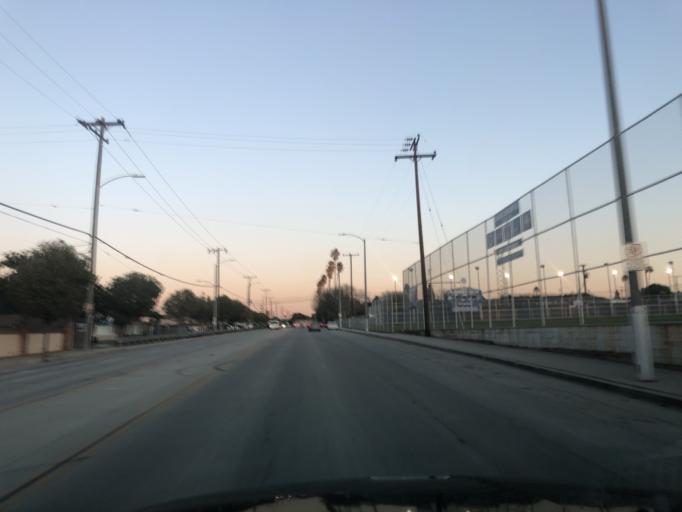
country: US
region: California
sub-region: Los Angeles County
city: Inglewood
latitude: 33.9562
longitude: -118.3309
